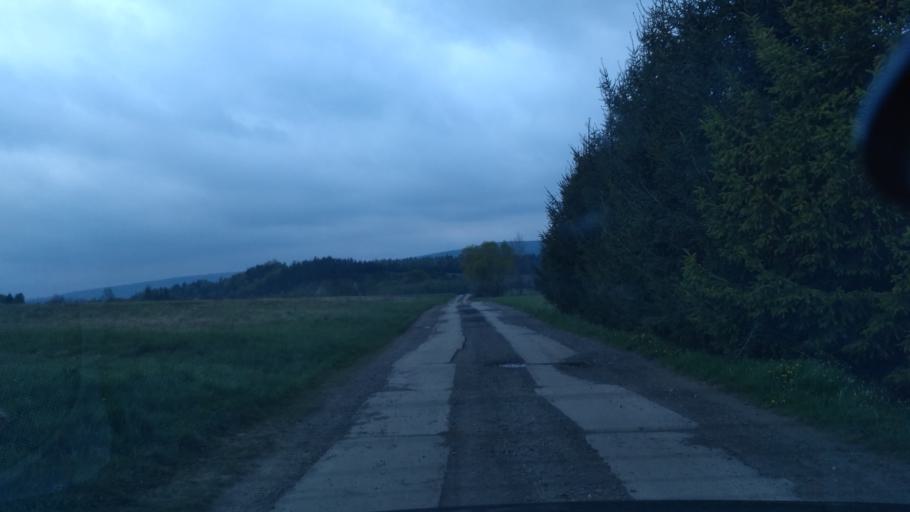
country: PL
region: Subcarpathian Voivodeship
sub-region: Powiat brzozowski
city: Dydnia
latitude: 49.6500
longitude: 22.2682
